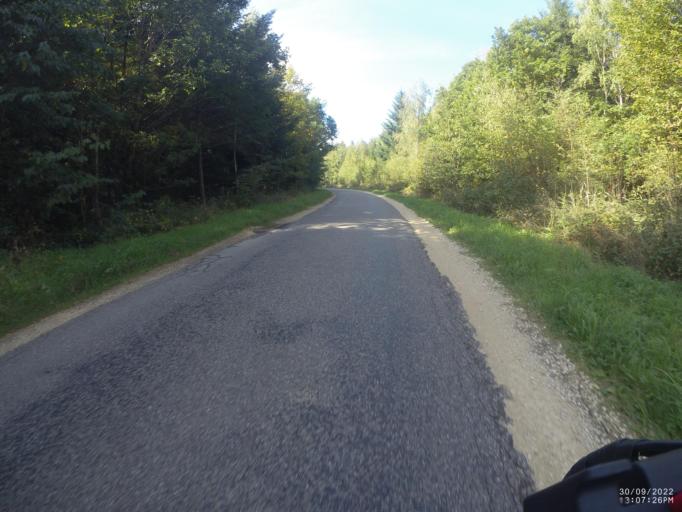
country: DE
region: Baden-Wuerttemberg
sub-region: Regierungsbezirk Stuttgart
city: Pluderhausen
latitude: 48.7802
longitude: 9.5869
